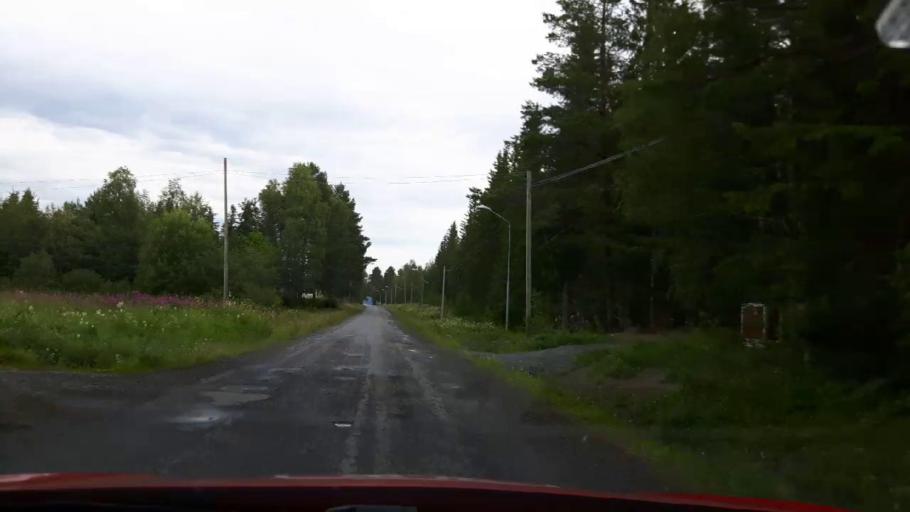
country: SE
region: Jaemtland
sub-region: Stroemsunds Kommun
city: Stroemsund
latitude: 63.5184
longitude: 15.3490
